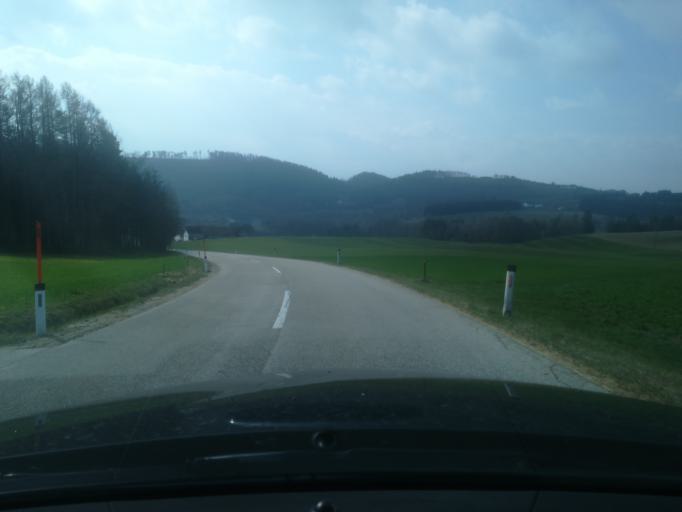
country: AT
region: Upper Austria
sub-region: Politischer Bezirk Perg
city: Perg
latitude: 48.3141
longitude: 14.6187
